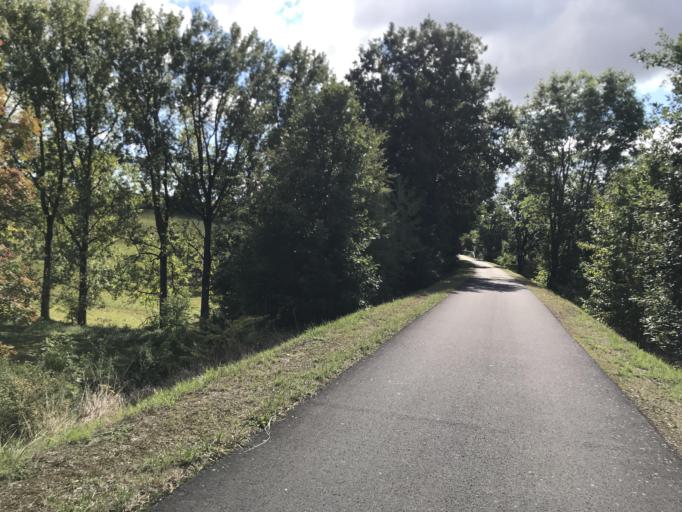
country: DE
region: Hesse
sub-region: Regierungsbezirk Kassel
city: Sachsenhausen
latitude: 51.2602
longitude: 8.9880
